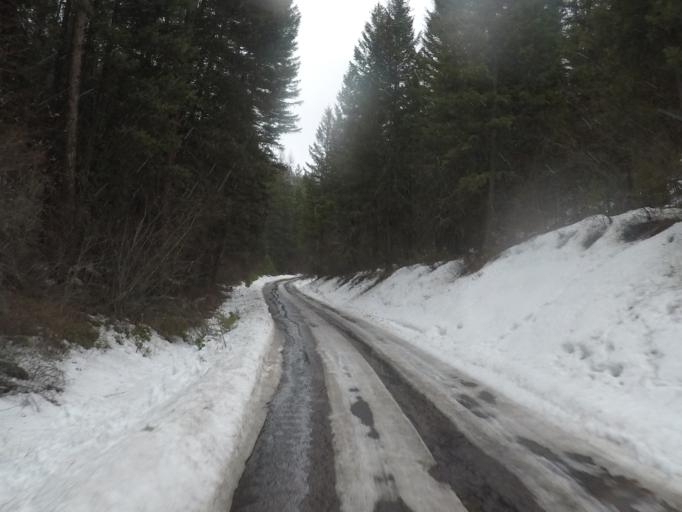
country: US
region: Montana
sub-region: Missoula County
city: Missoula
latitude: 46.9308
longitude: -113.9719
